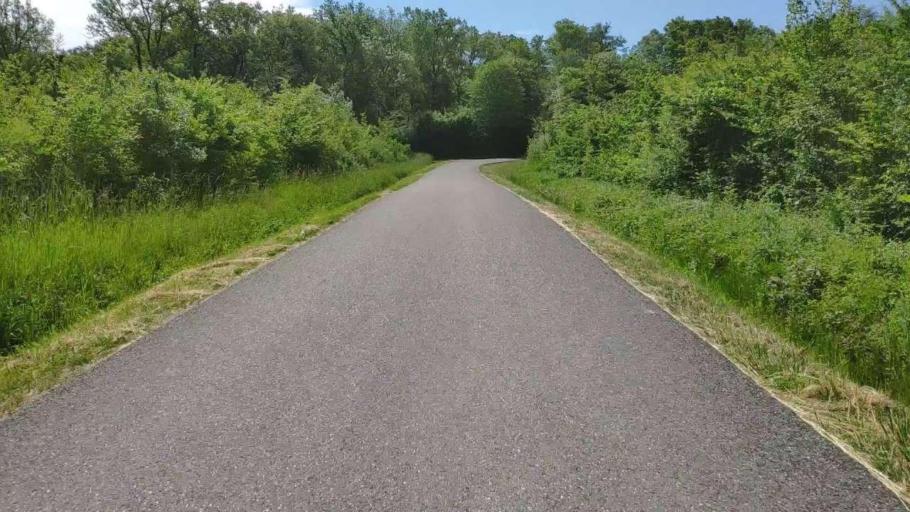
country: FR
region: Franche-Comte
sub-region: Departement du Jura
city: Bletterans
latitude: 46.7114
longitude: 5.4085
